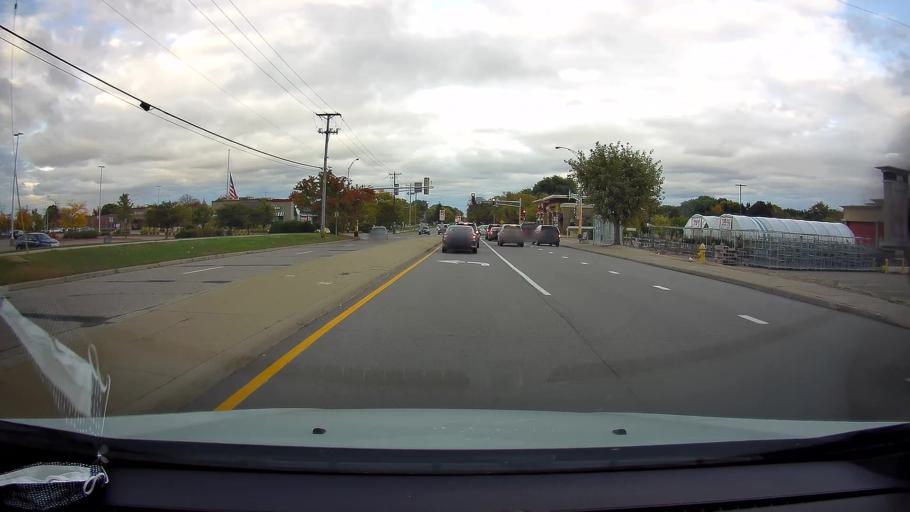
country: US
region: Minnesota
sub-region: Ramsey County
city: Roseville
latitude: 45.0062
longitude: -93.1642
